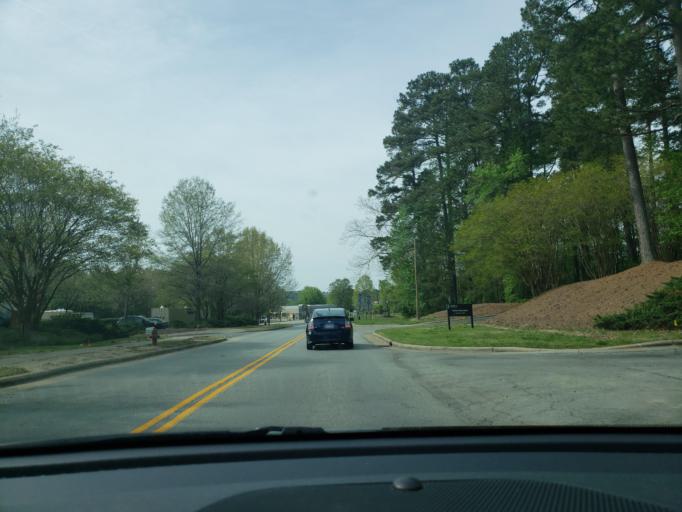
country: US
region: North Carolina
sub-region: Durham County
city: Durham
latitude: 35.9723
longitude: -78.9580
